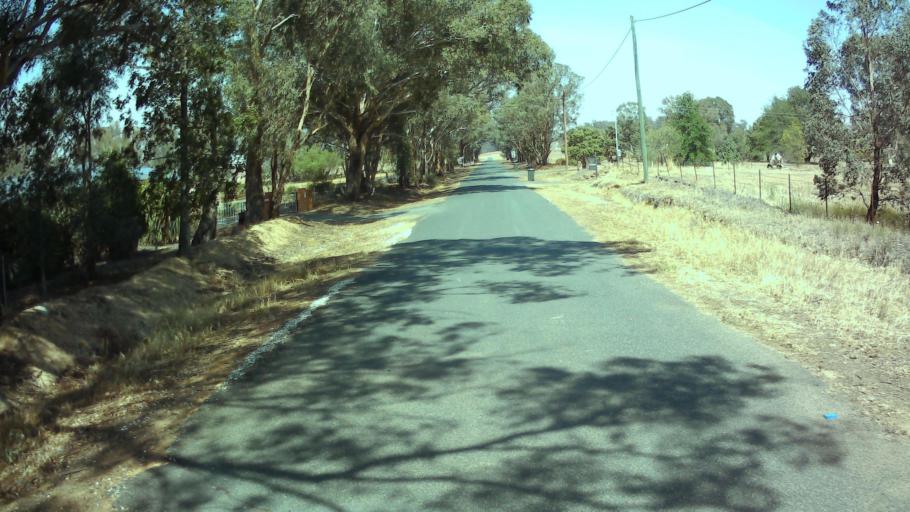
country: AU
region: New South Wales
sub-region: Weddin
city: Grenfell
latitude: -33.8956
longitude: 148.1451
